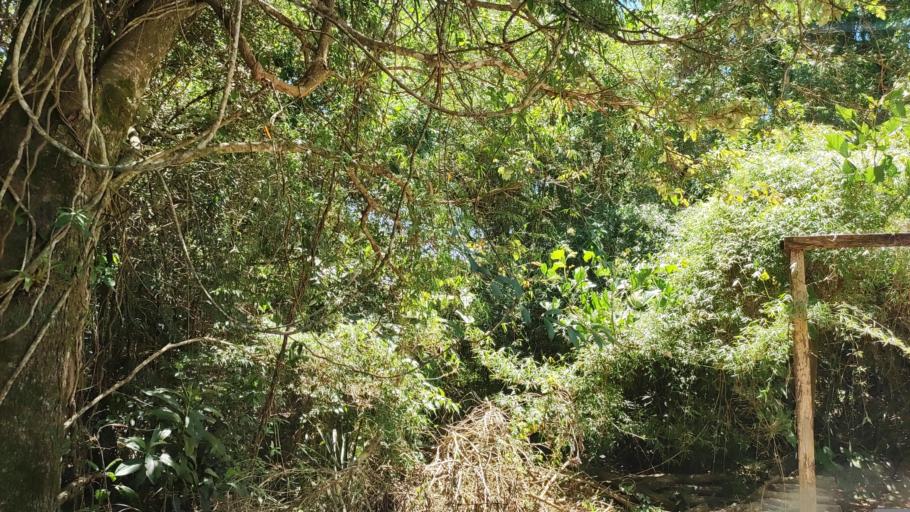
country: AR
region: Misiones
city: Dos de Mayo
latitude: -26.9995
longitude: -54.6287
